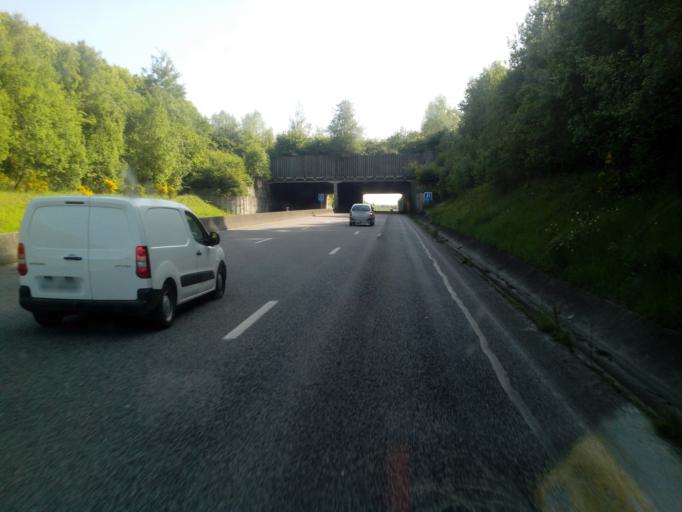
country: FR
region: Haute-Normandie
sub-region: Departement de la Seine-Maritime
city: Blangy-sur-Bresle
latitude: 49.8928
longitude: 1.6042
